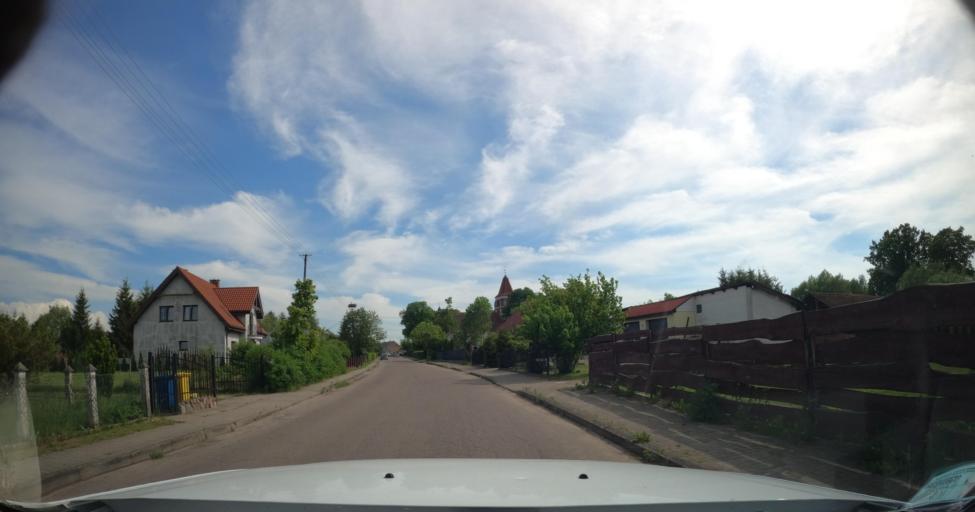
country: PL
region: Warmian-Masurian Voivodeship
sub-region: Powiat lidzbarski
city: Lubomino
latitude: 54.0688
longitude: 20.2391
